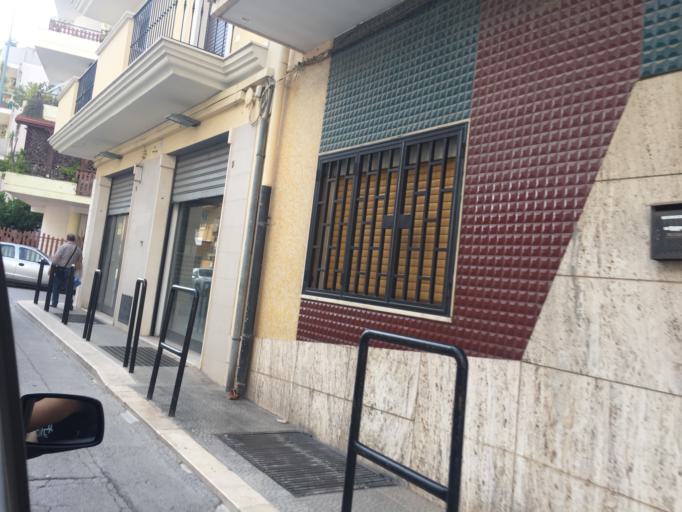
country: IT
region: Apulia
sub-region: Provincia di Bari
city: Capurso
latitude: 41.0480
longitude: 16.9176
